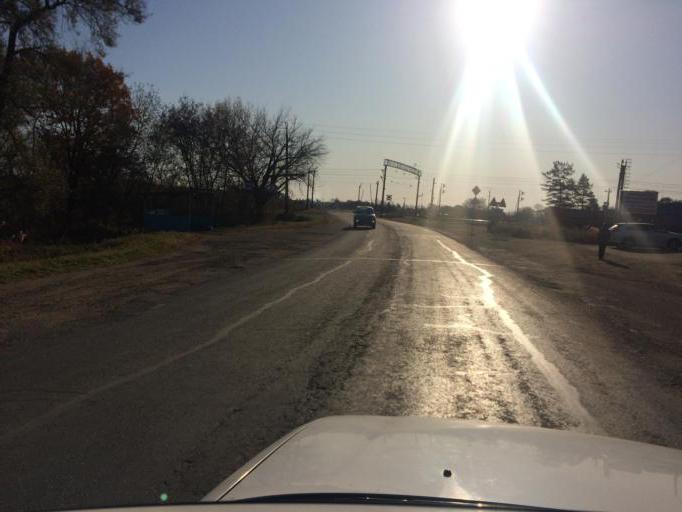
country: RU
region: Primorskiy
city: Dal'nerechensk
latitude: 45.9126
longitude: 133.7929
